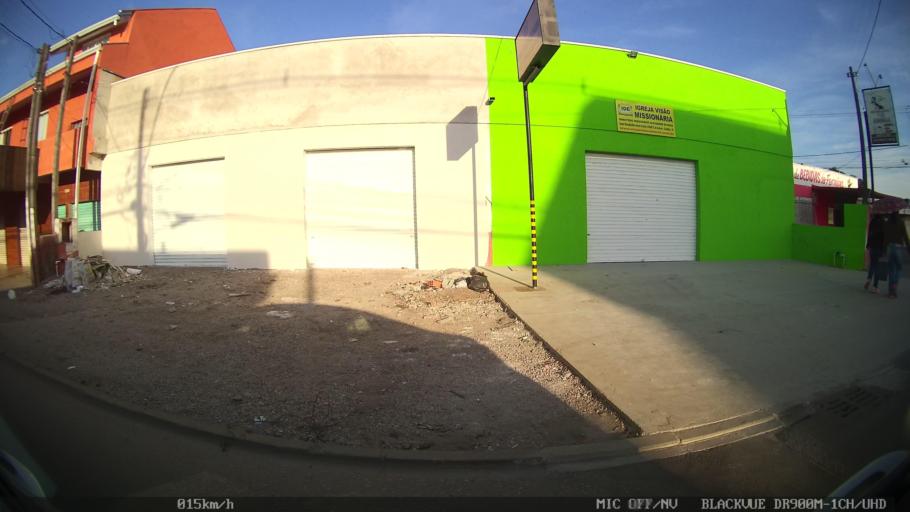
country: BR
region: Parana
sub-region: Pinhais
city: Pinhais
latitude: -25.4520
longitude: -49.1484
